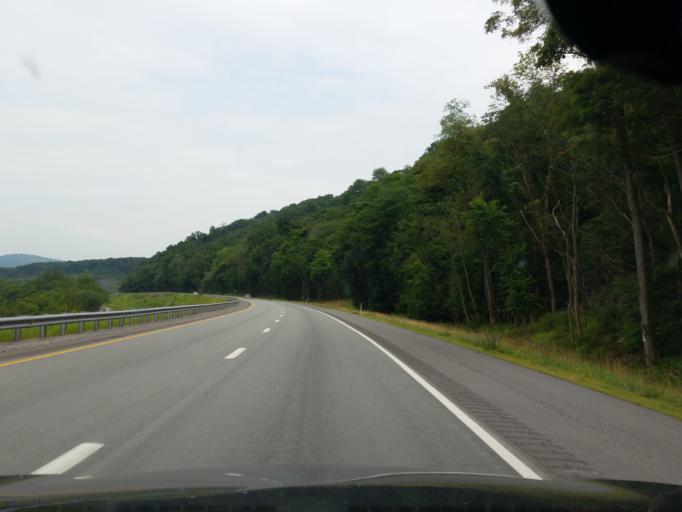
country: US
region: Pennsylvania
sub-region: Perry County
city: Duncannon
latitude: 40.4732
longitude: -77.0335
